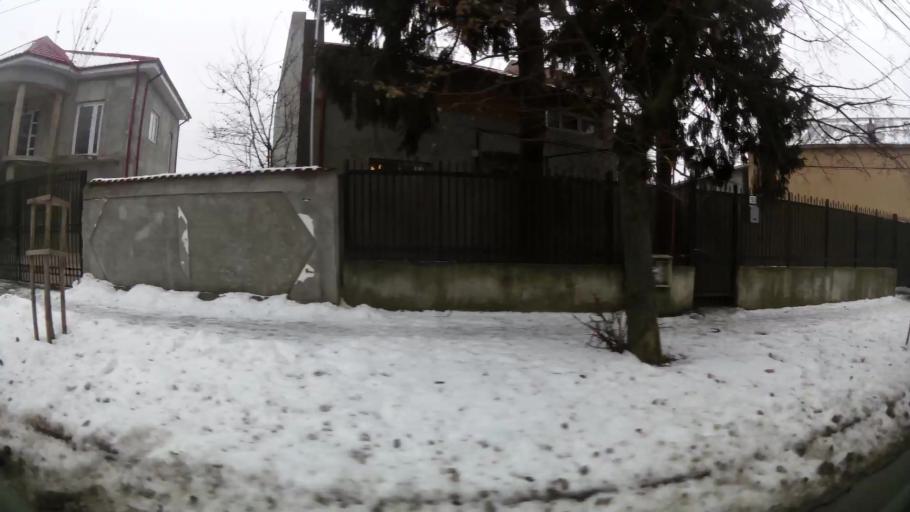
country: RO
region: Ilfov
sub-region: Comuna Chiajna
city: Rosu
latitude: 44.4699
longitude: 26.0036
